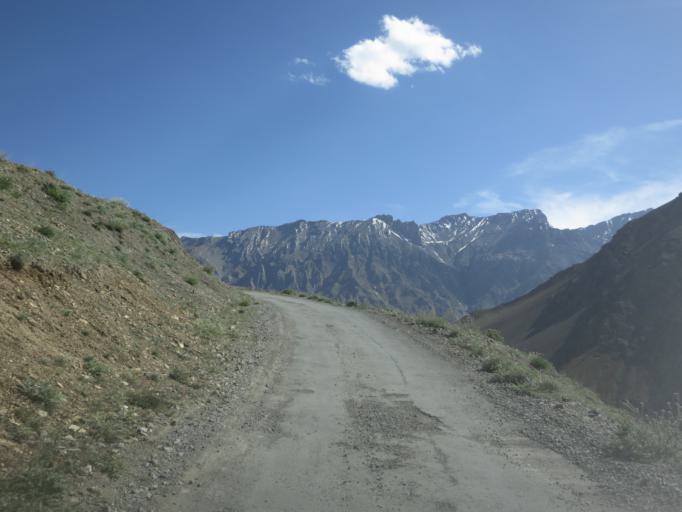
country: IN
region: Himachal Pradesh
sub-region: Kulu
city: Manali
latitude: 32.3247
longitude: 78.0042
